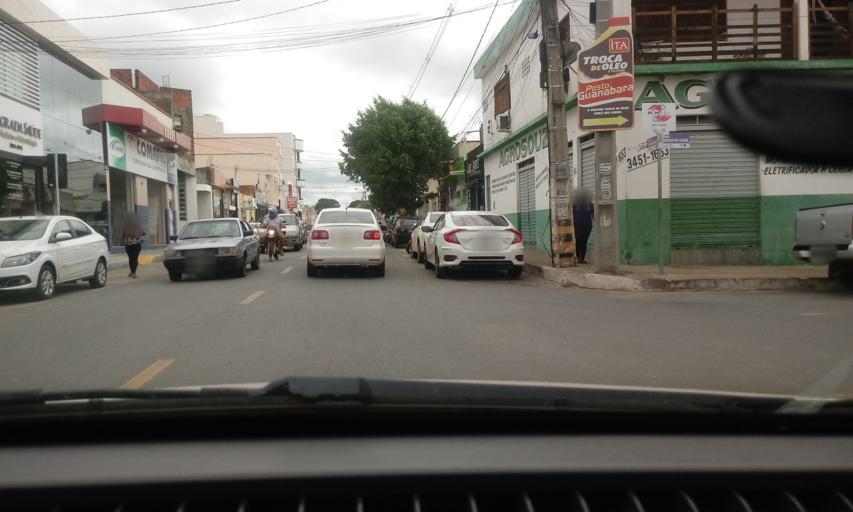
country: BR
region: Bahia
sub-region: Guanambi
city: Guanambi
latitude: -14.2213
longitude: -42.7799
